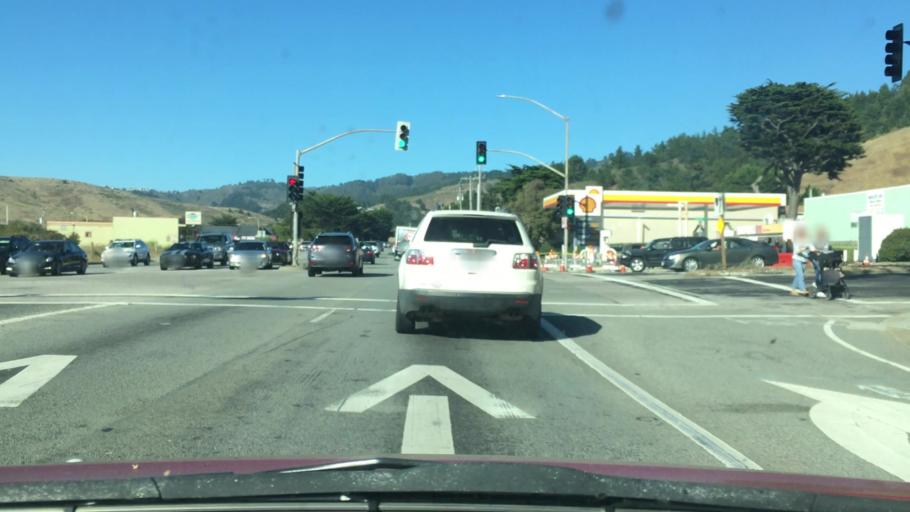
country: US
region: California
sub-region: San Mateo County
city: Pacifica
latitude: 37.6093
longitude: -122.4965
